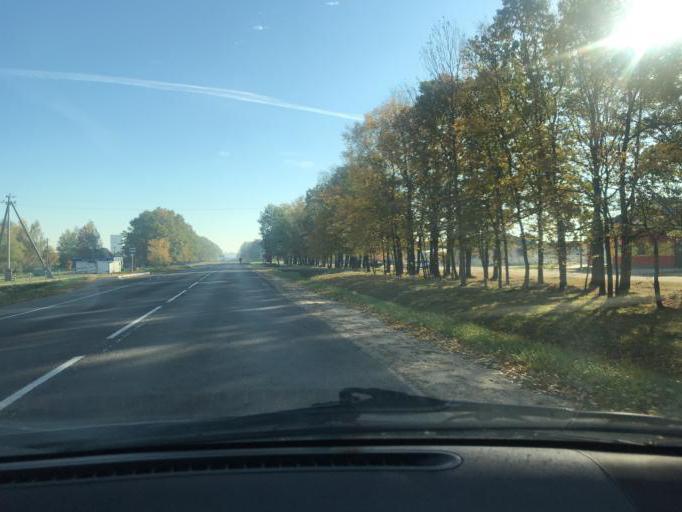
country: BY
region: Brest
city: Ivanava
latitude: 52.1439
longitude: 25.5044
